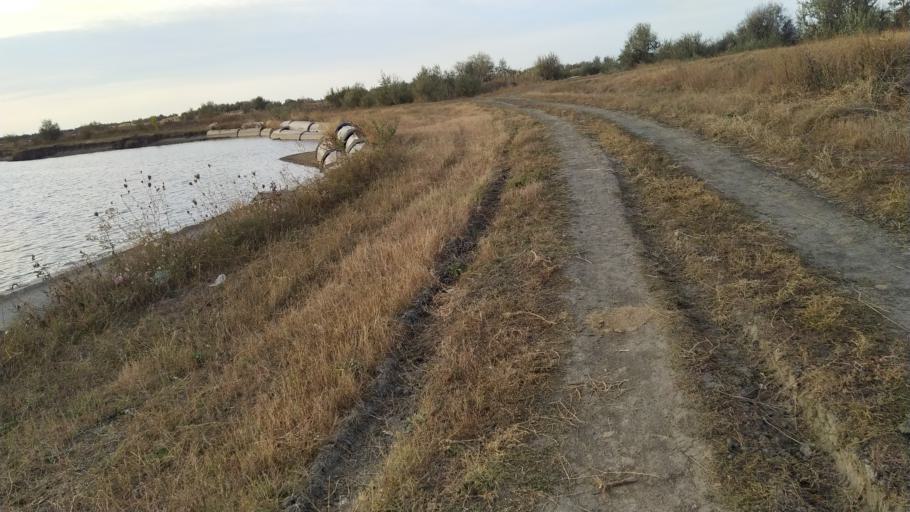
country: RU
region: Rostov
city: Kuleshovka
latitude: 47.1208
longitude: 39.6300
